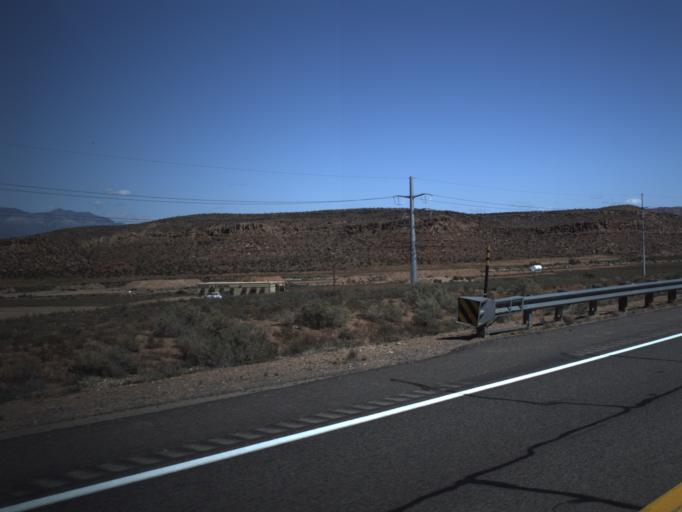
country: US
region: Utah
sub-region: Washington County
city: Saint George
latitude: 37.0083
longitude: -113.5150
